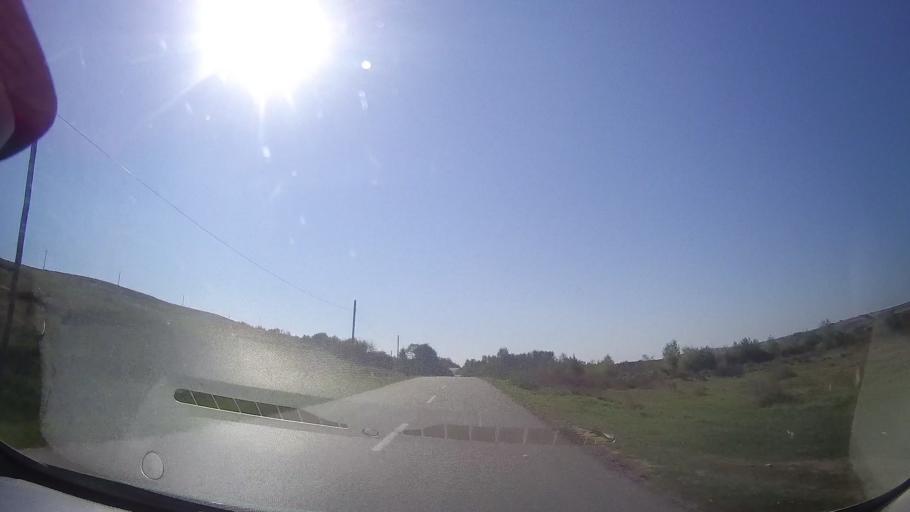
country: RO
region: Timis
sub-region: Comuna Bethausen
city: Bethausen
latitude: 45.8562
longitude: 21.9672
